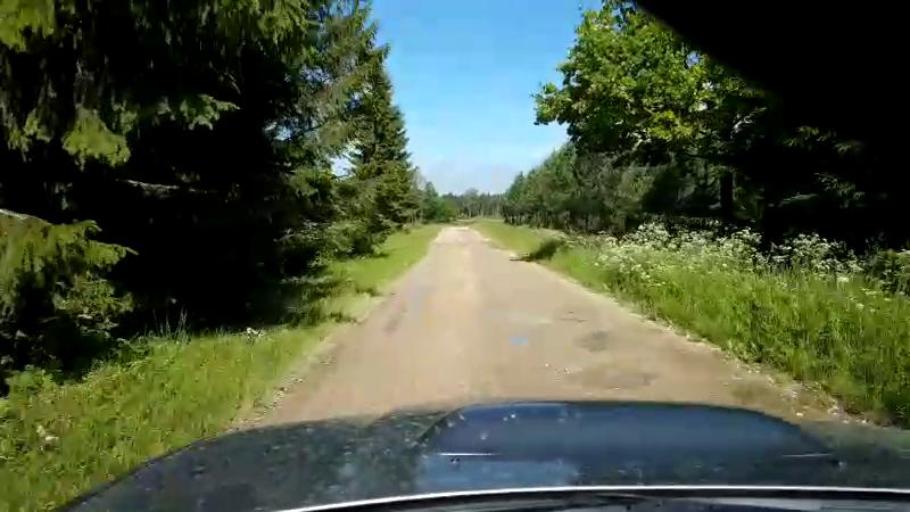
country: EE
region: Paernumaa
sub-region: Sindi linn
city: Sindi
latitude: 58.5100
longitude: 24.6885
